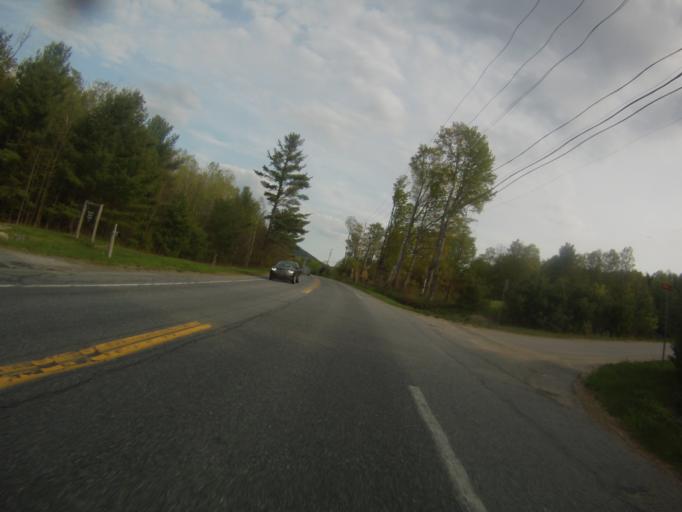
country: US
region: New York
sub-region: Warren County
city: Warrensburg
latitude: 43.6507
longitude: -73.9506
